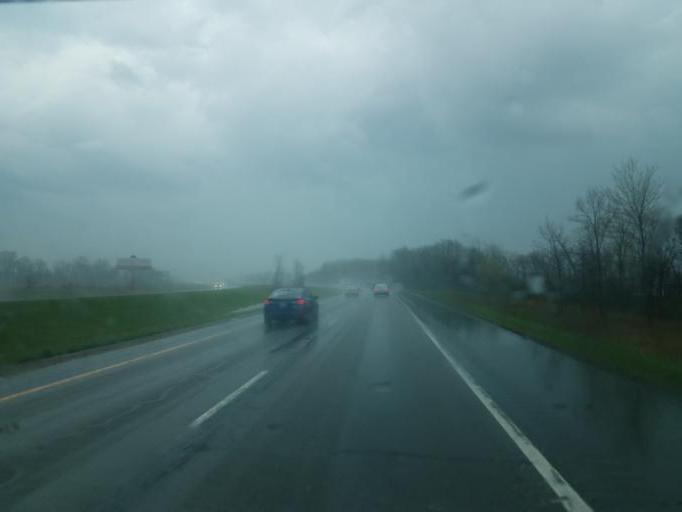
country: US
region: Michigan
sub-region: Livingston County
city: Fowlerville
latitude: 42.6470
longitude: -84.1026
